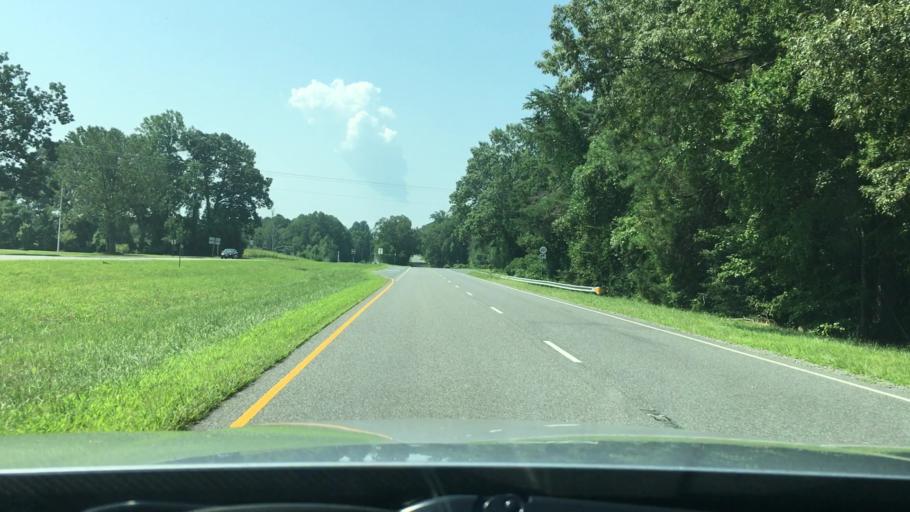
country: US
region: Virginia
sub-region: Caroline County
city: Bowling Green
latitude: 38.0000
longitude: -77.4162
